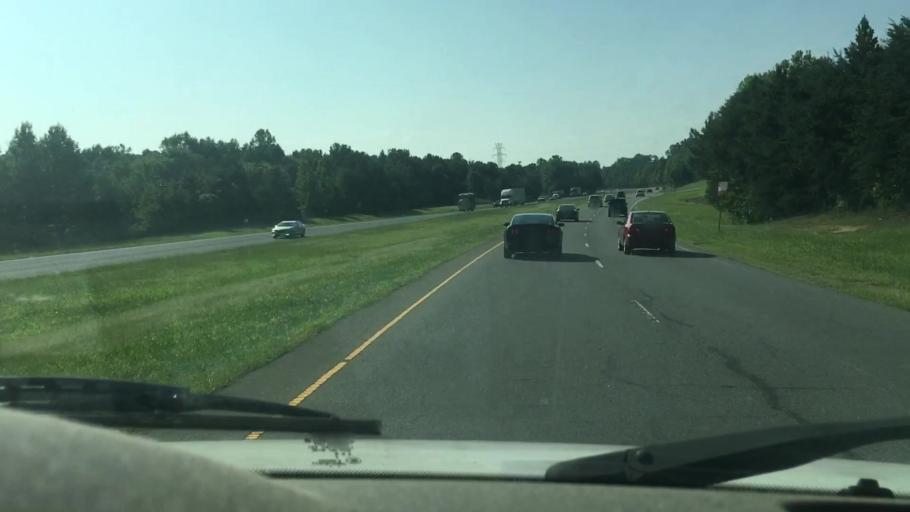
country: US
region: North Carolina
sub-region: Gaston County
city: Mount Holly
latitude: 35.3467
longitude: -80.9694
